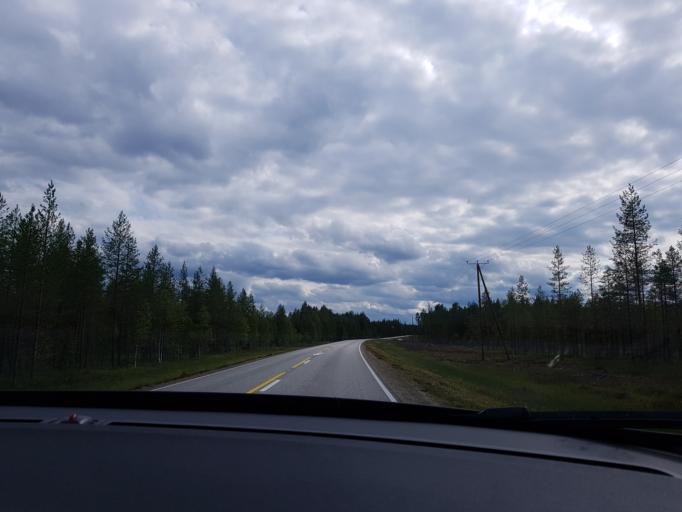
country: FI
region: Kainuu
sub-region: Kehys-Kainuu
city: Kuhmo
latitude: 64.3347
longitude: 29.8774
